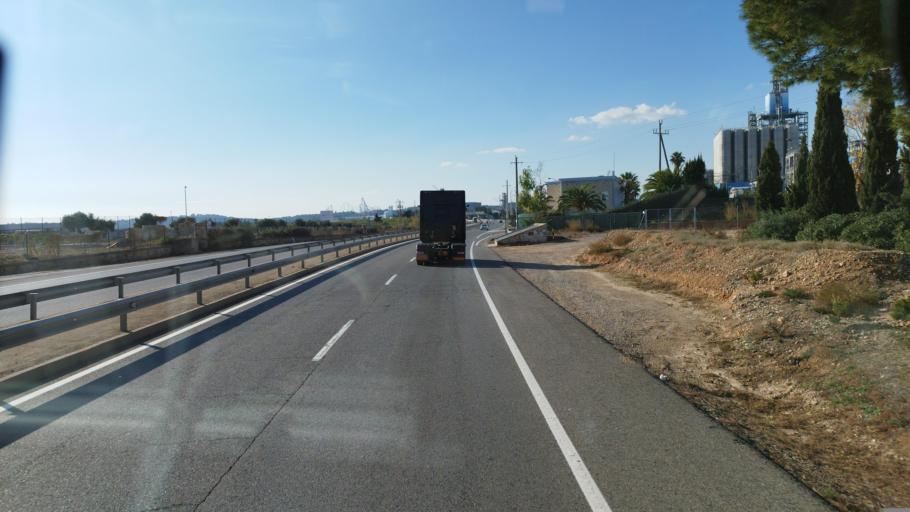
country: ES
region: Catalonia
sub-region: Provincia de Barcelona
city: La Pineda
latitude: 41.1025
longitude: 1.1930
